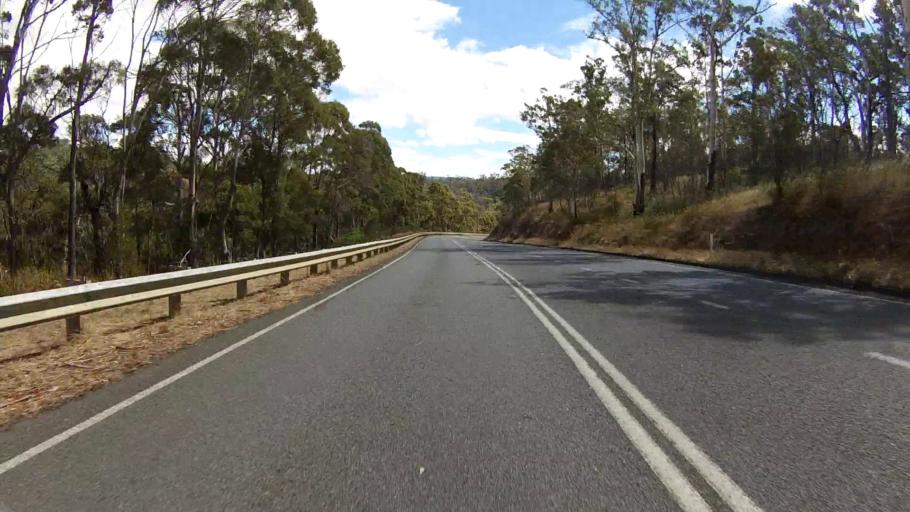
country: AU
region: Tasmania
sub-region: Sorell
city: Sorell
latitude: -42.6112
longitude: 147.6462
